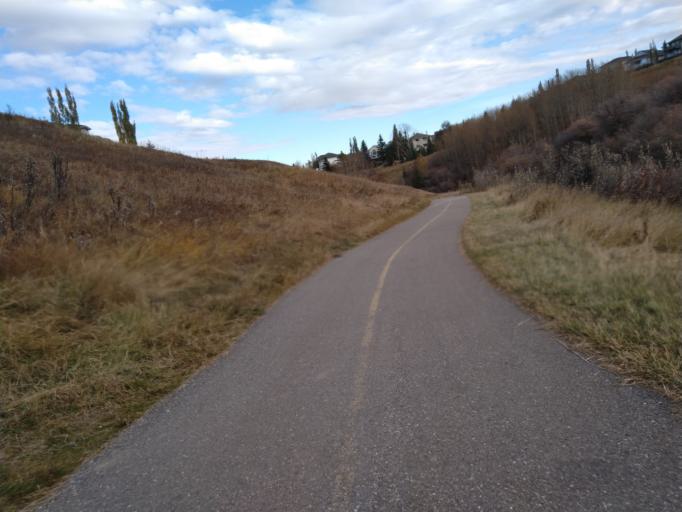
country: CA
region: Alberta
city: Calgary
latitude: 51.1364
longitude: -114.1404
